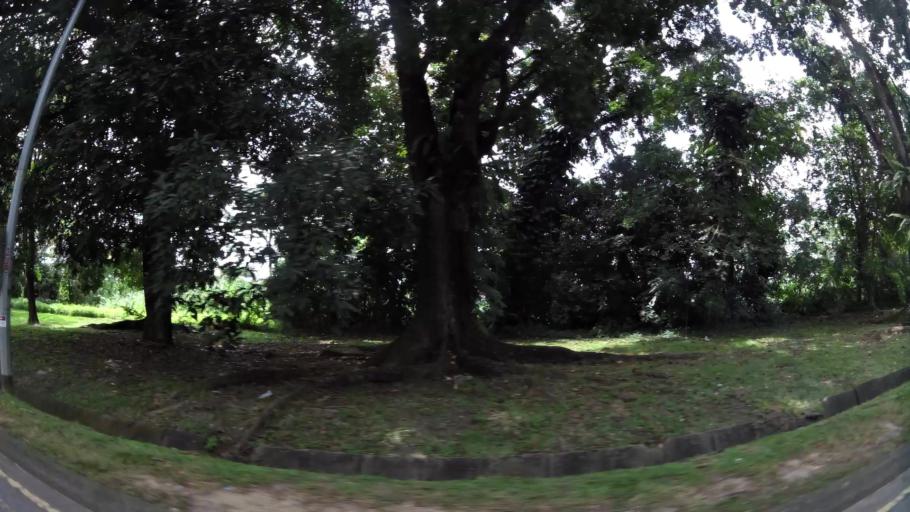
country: MY
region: Johor
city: Johor Bahru
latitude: 1.4194
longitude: 103.7546
